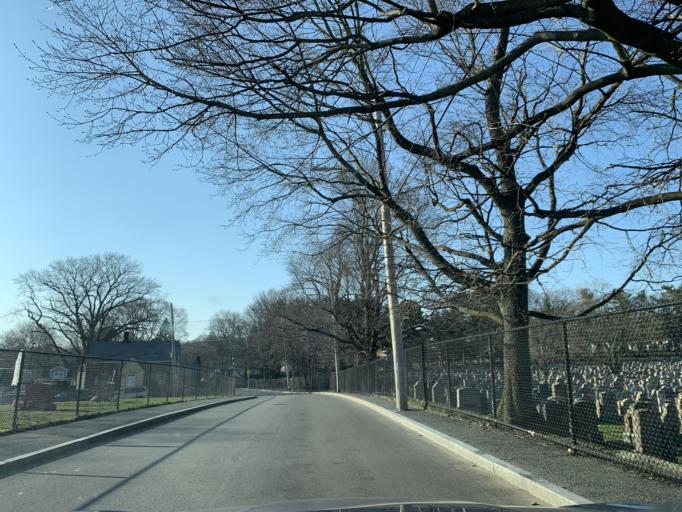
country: US
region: Massachusetts
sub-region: Suffolk County
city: Jamaica Plain
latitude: 42.2878
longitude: -71.1112
